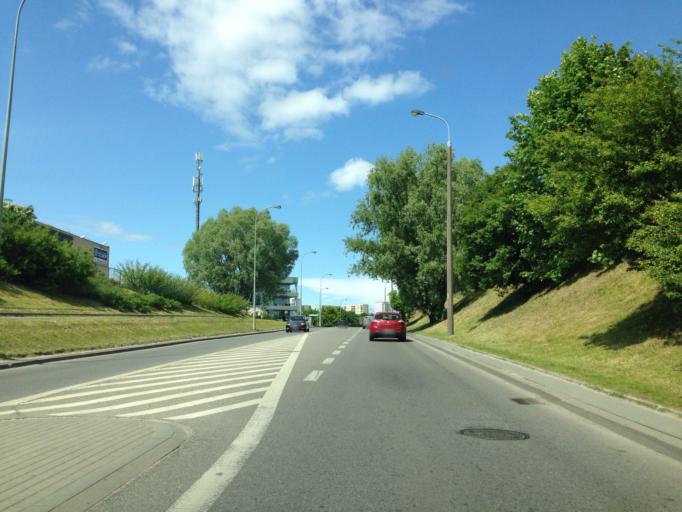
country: PL
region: Pomeranian Voivodeship
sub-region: Gdansk
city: Gdansk
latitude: 54.3527
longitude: 18.5962
